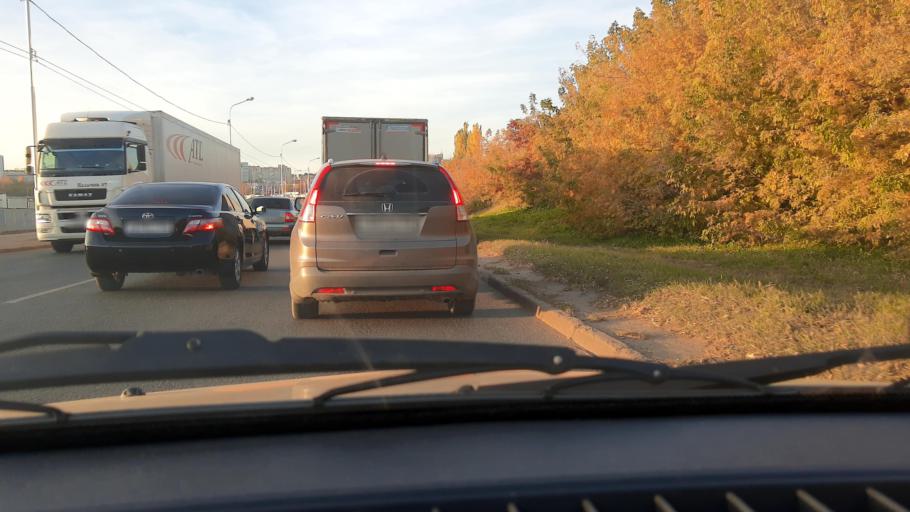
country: RU
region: Bashkortostan
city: Ufa
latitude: 54.7065
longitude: 55.9665
